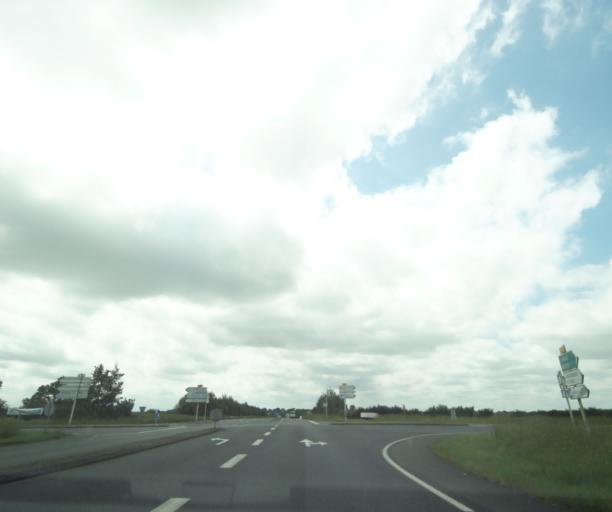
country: FR
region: Poitou-Charentes
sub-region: Departement des Deux-Sevres
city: Viennay
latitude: 46.7748
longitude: -0.2191
